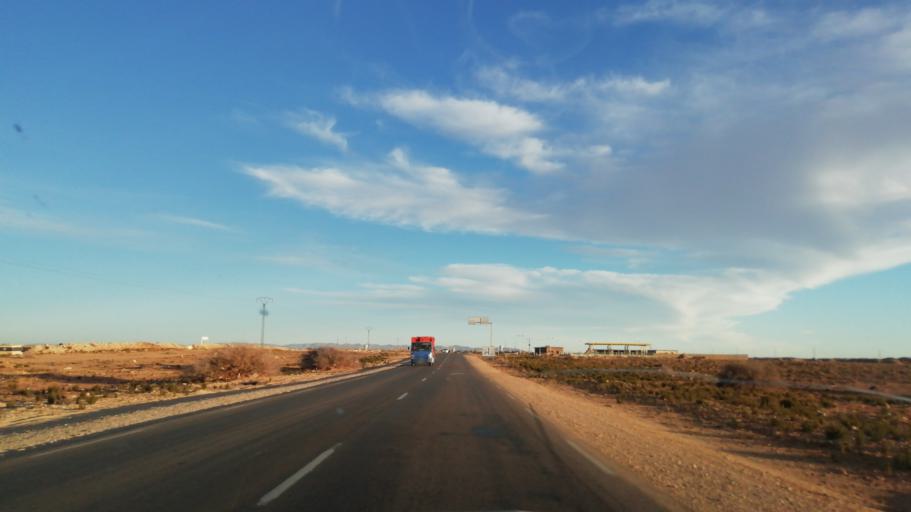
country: DZ
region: Wilaya de Naama
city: Naama
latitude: 33.7275
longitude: -0.7465
